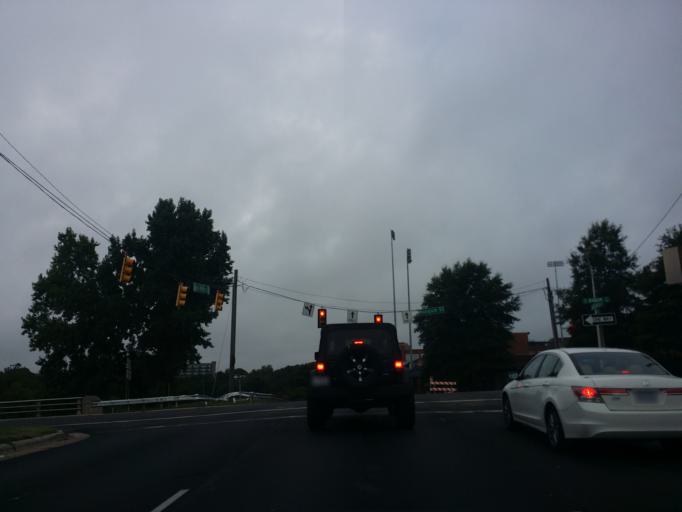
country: US
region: North Carolina
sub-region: Durham County
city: Durham
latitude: 35.9904
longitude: -78.9026
